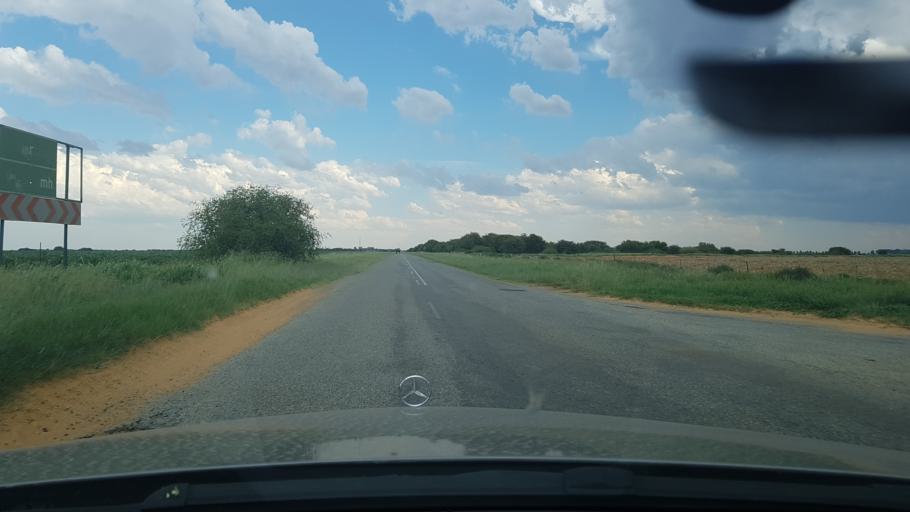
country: ZA
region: Orange Free State
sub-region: Lejweleputswa District Municipality
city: Hoopstad
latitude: -27.9284
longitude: 25.6898
